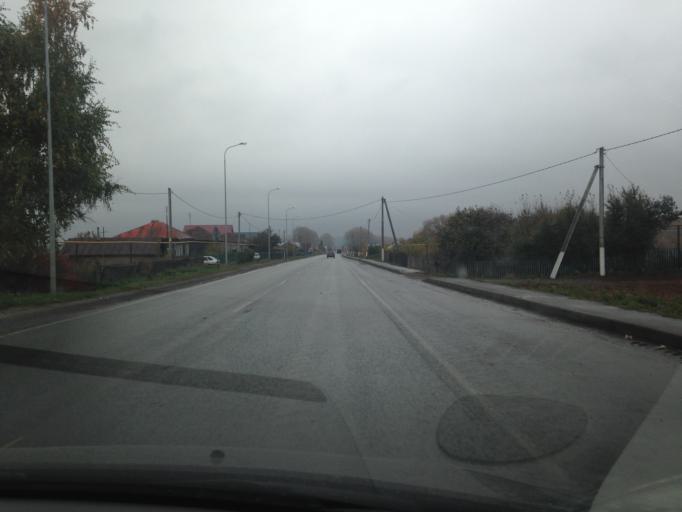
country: RU
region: Tatarstan
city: Buinsk
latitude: 54.9946
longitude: 48.3314
